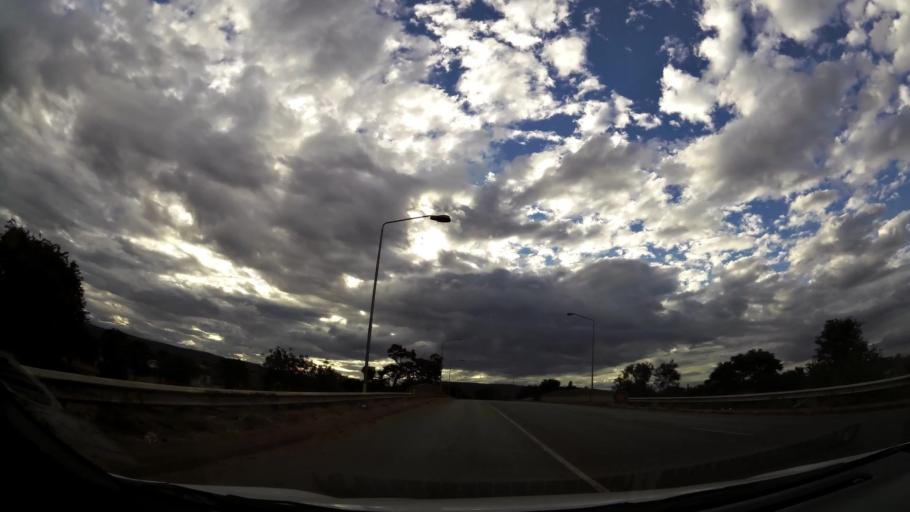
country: ZA
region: Limpopo
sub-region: Waterberg District Municipality
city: Modimolle
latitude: -24.5252
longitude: 28.7101
